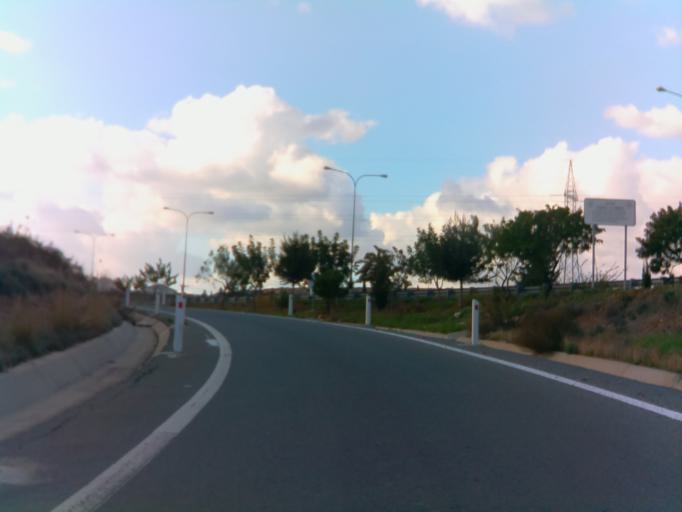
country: CY
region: Pafos
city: Paphos
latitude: 34.7463
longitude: 32.5027
